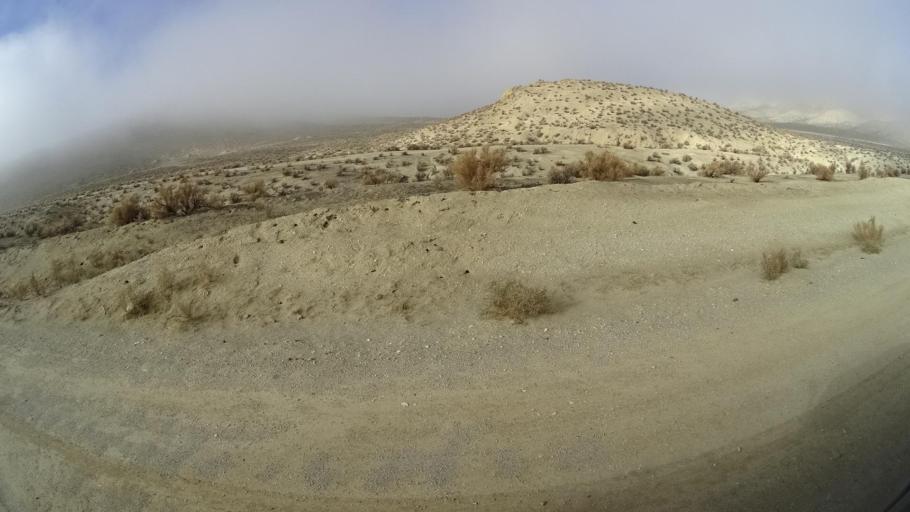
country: US
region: California
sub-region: Kern County
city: Maricopa
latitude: 35.0292
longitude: -119.4409
